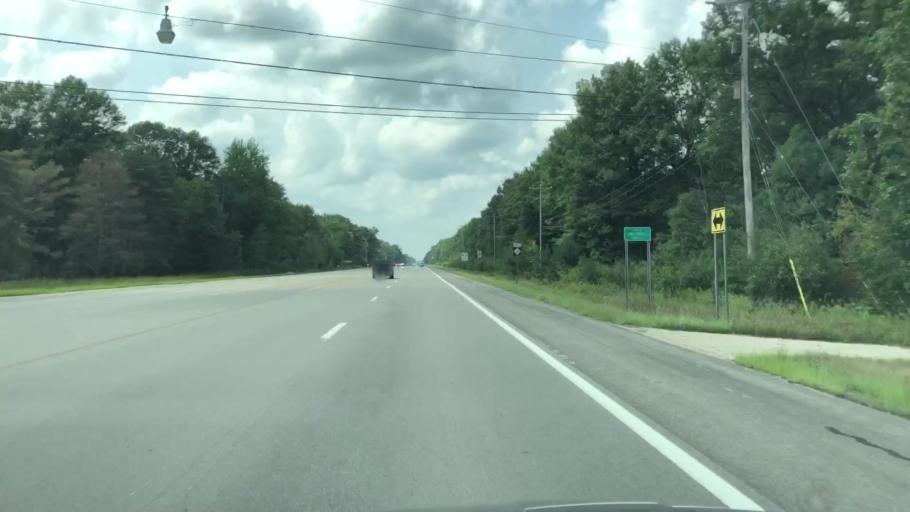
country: US
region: Michigan
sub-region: Midland County
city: Coleman
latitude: 43.6115
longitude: -84.4883
